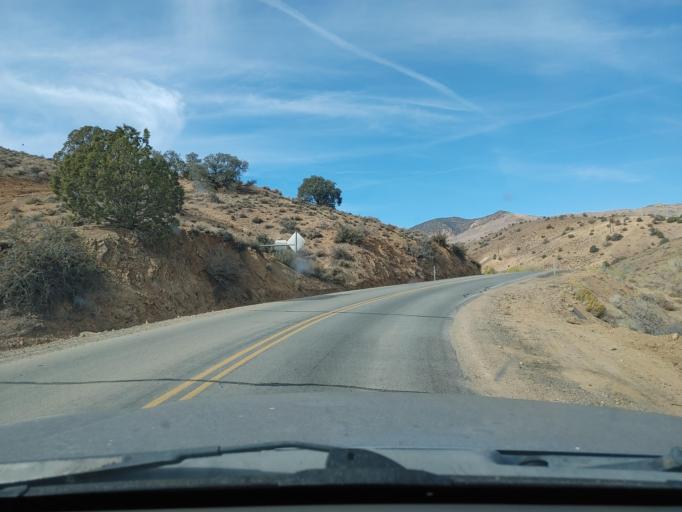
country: US
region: Nevada
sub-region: Lyon County
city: Dayton
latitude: 39.3064
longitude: -119.5706
